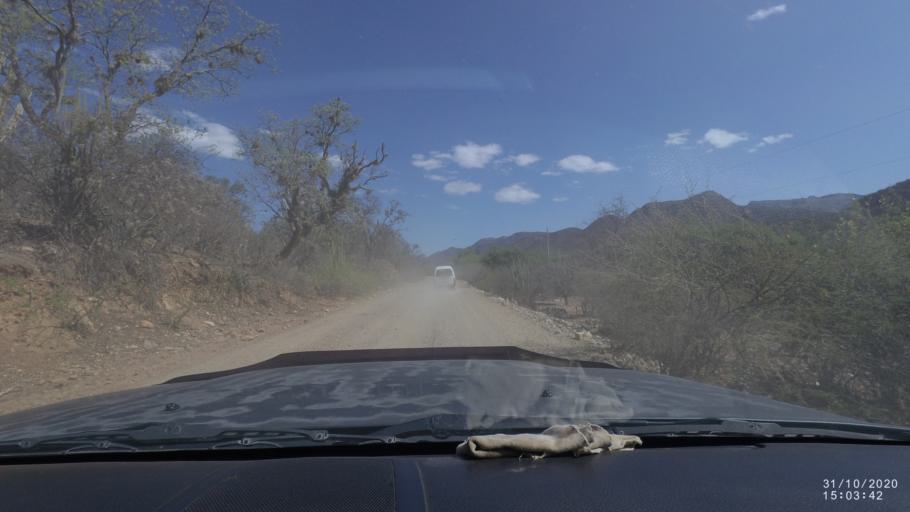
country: BO
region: Cochabamba
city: Aiquile
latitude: -18.2771
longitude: -64.8051
